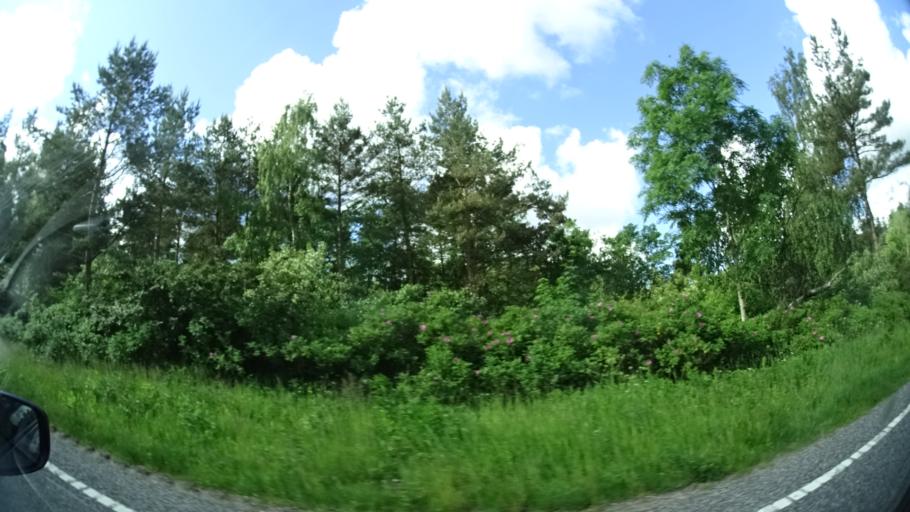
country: DK
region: Central Jutland
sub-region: Syddjurs Kommune
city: Ebeltoft
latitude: 56.2580
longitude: 10.6260
